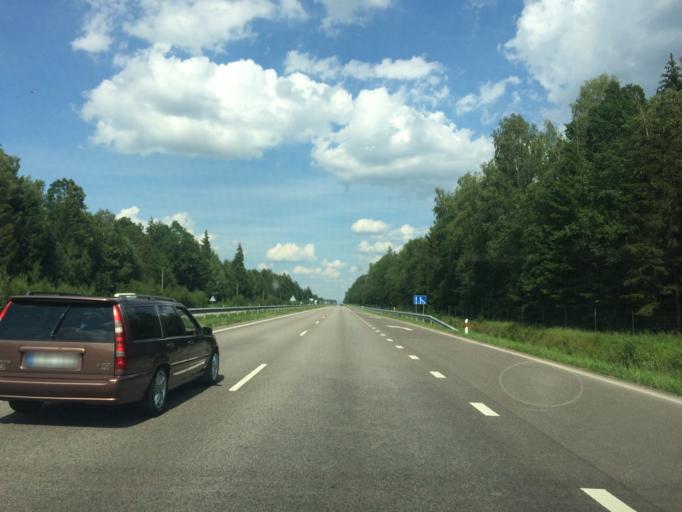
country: LT
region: Kauno apskritis
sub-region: Kauno rajonas
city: Karmelava
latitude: 55.0161
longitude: 24.1685
